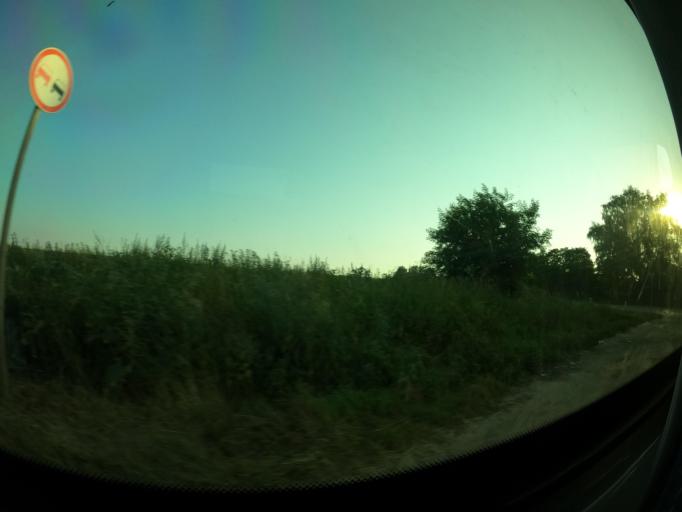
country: RU
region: Moskovskaya
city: Serpukhov
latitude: 54.9376
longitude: 37.3610
